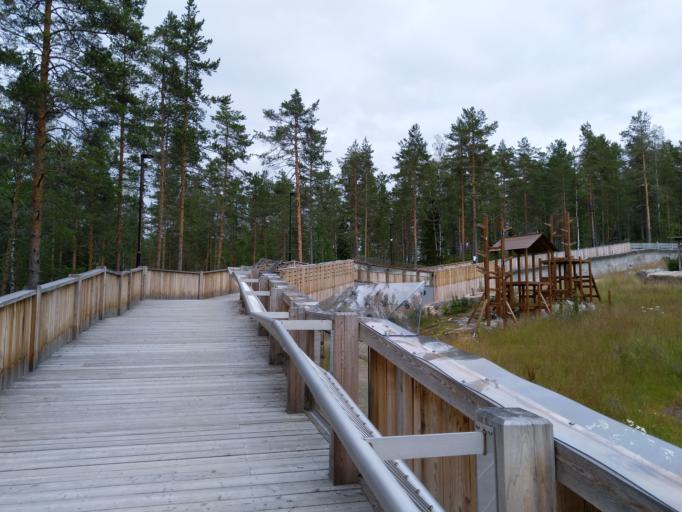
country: FI
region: Southern Ostrobothnia
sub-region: Kuusiokunnat
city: AEhtaeri
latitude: 62.5373
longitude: 24.1831
